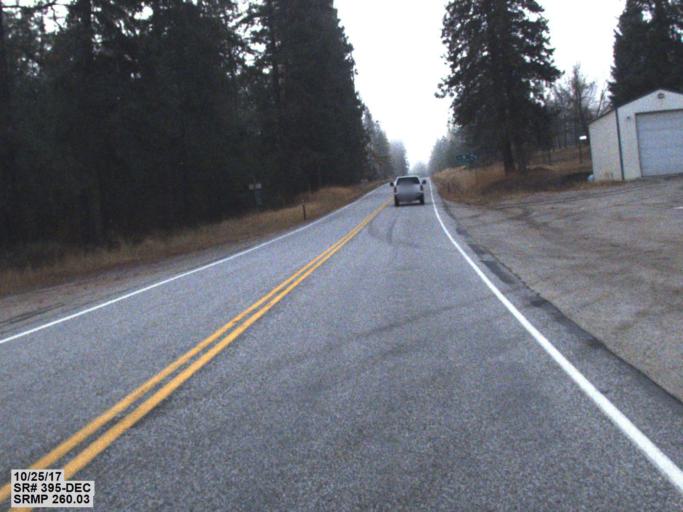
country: CA
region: British Columbia
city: Grand Forks
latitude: 48.8632
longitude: -118.2053
